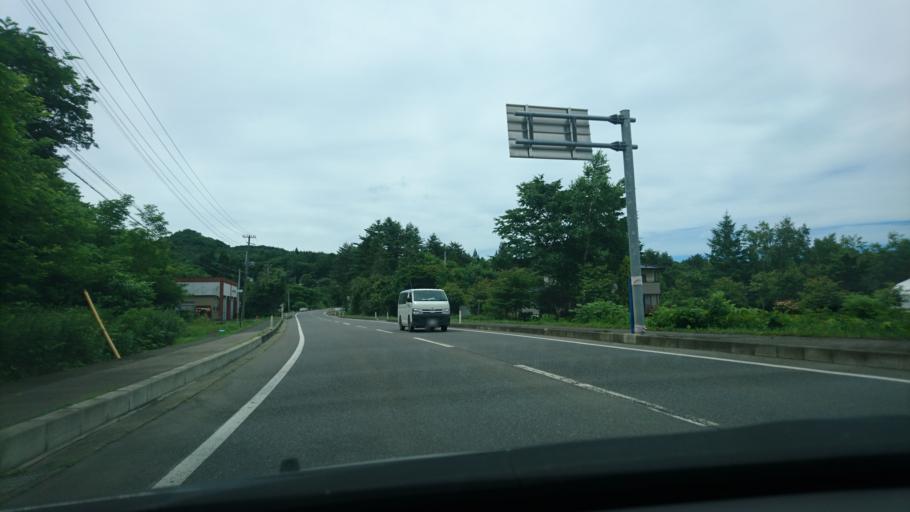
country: JP
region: Iwate
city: Miyako
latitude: 39.9153
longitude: 141.9049
